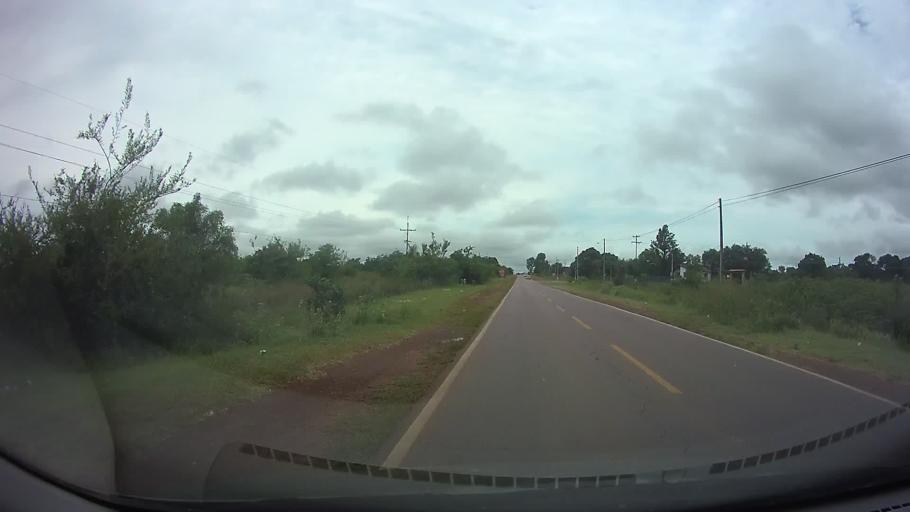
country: PY
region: Paraguari
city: Carapegua
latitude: -25.7759
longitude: -57.2286
